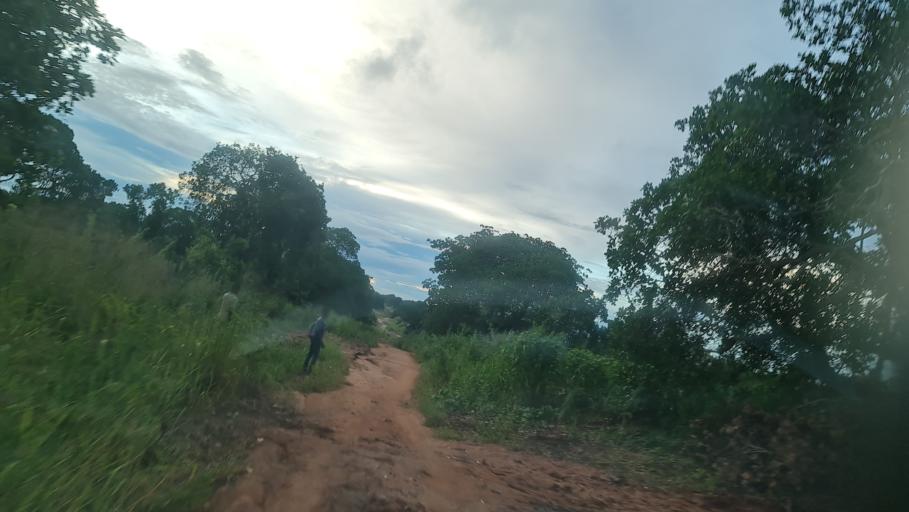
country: MZ
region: Nampula
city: Nampula
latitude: -14.7397
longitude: 39.9331
